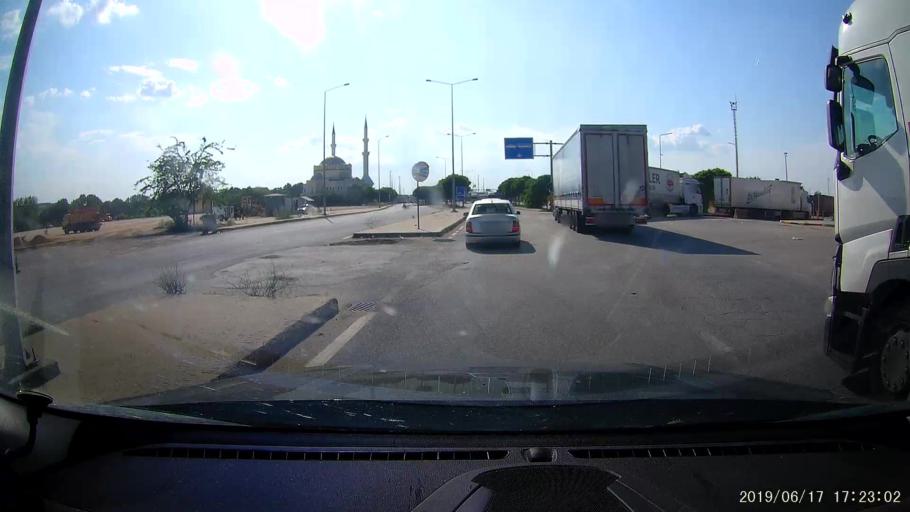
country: GR
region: East Macedonia and Thrace
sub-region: Nomos Evrou
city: Rizia
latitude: 41.7134
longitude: 26.3682
